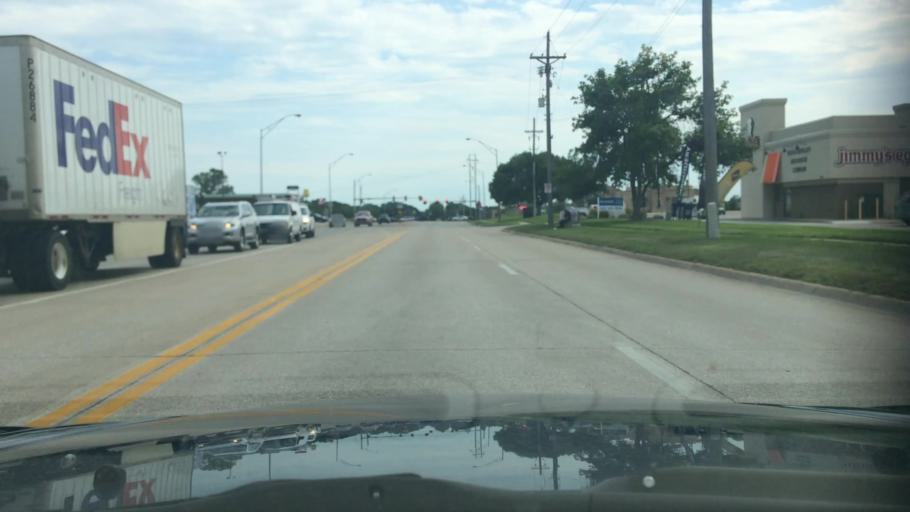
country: US
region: Nebraska
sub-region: Douglas County
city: Ralston
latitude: 41.2075
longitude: -96.0815
